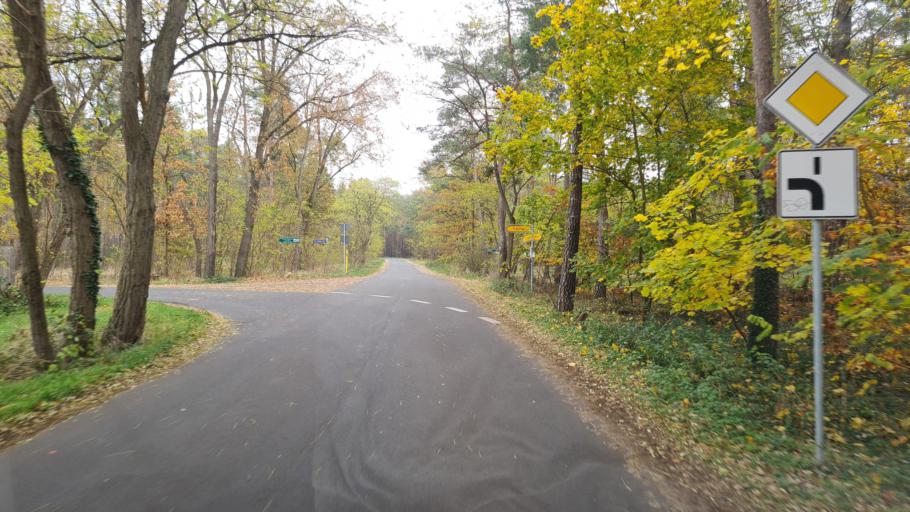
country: DE
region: Brandenburg
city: Gross Kreutz
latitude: 52.3419
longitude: 12.7348
